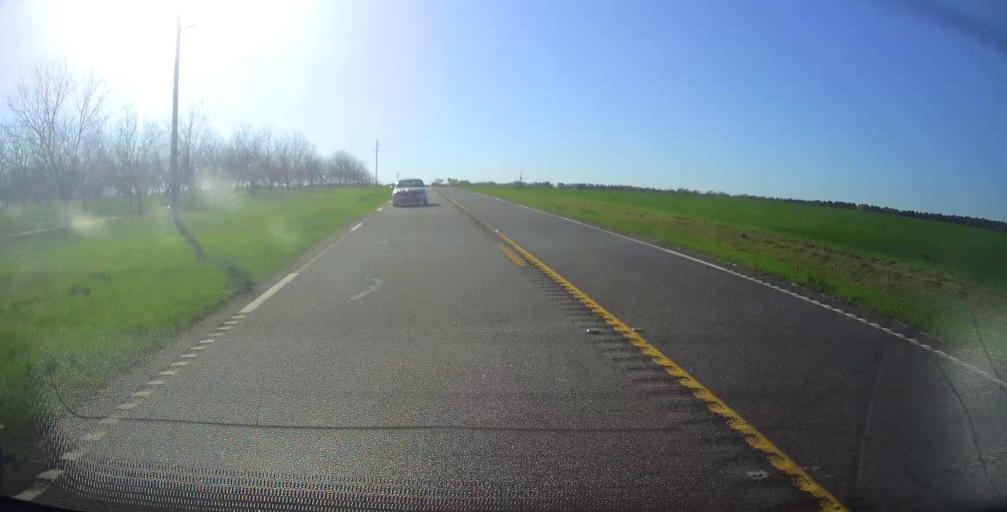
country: US
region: Georgia
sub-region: Macon County
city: Marshallville
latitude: 32.4395
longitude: -83.8713
